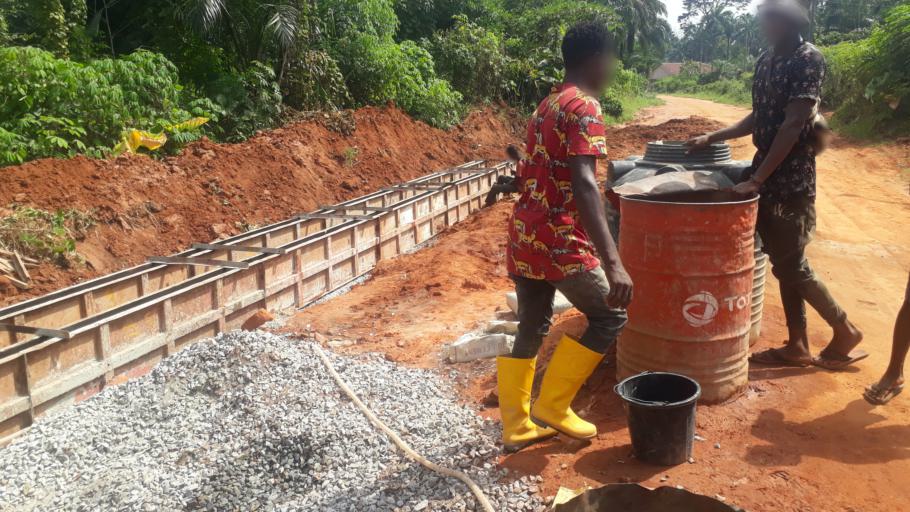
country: NG
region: Imo
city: Ihuo
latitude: 5.5323
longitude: 7.2581
